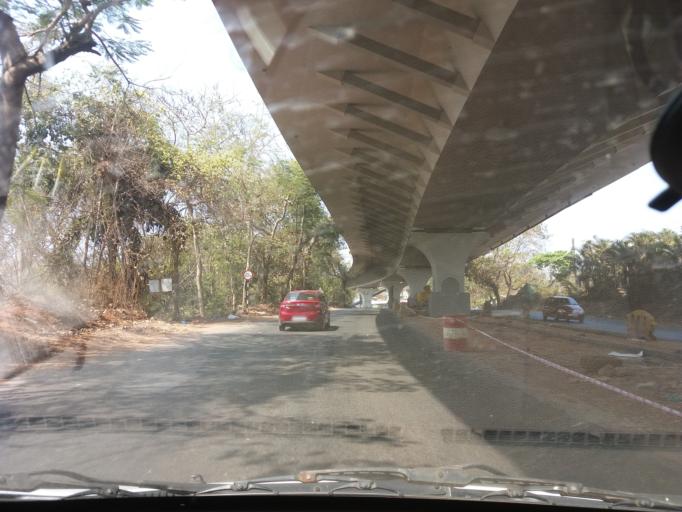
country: IN
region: Goa
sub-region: North Goa
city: Panaji
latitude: 15.5124
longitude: 73.8348
